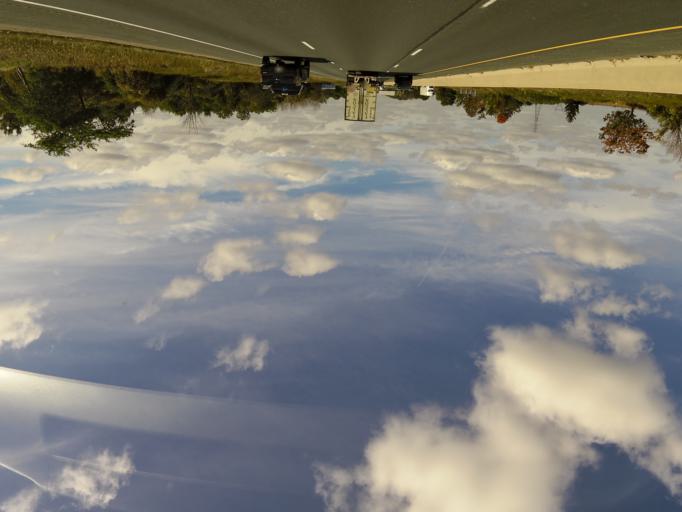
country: CA
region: Ontario
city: London
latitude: 42.9397
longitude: -81.1582
